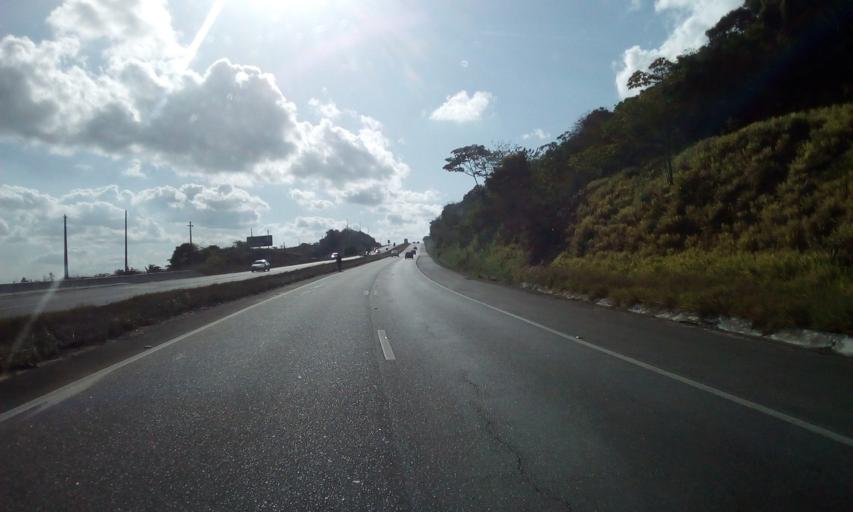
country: BR
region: Paraiba
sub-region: Santa Rita
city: Santa Rita
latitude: -7.1414
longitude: -34.9779
